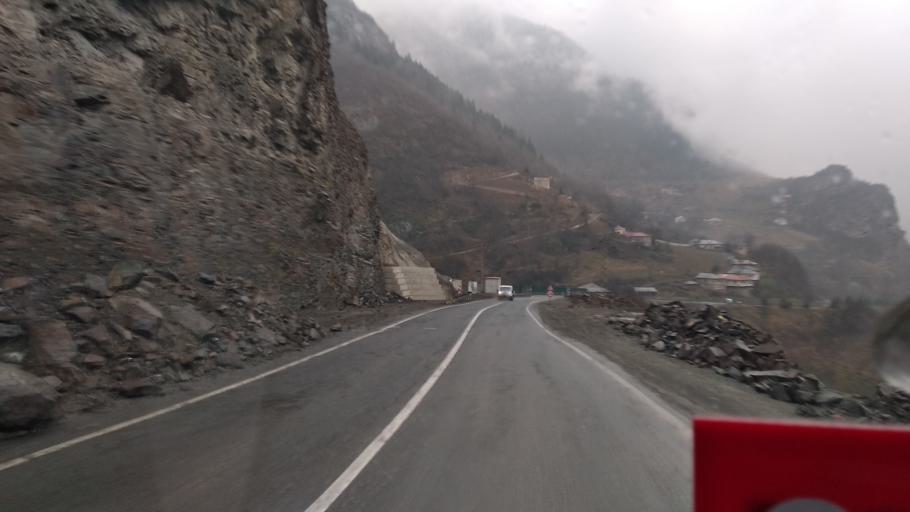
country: TR
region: Trabzon
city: Macka
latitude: 40.7249
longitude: 39.5229
